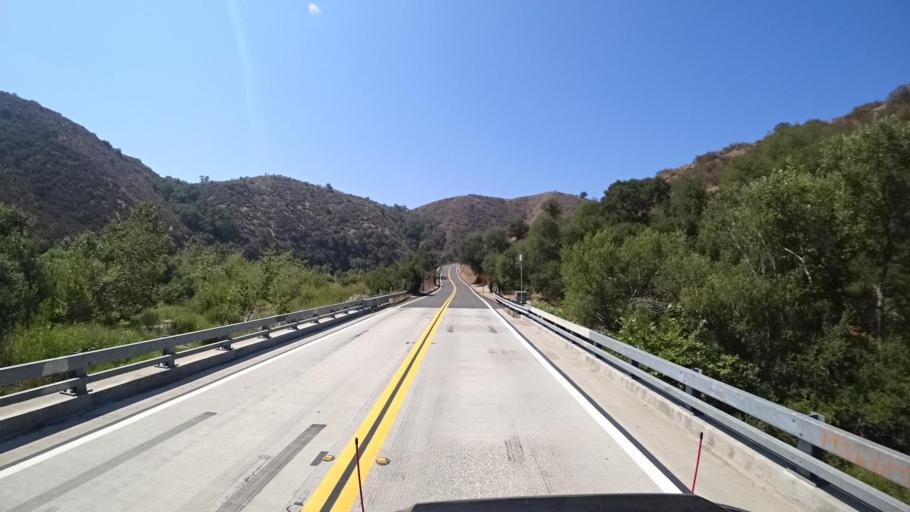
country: US
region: California
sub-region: San Diego County
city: Fallbrook
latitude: 33.3981
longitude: -117.2627
